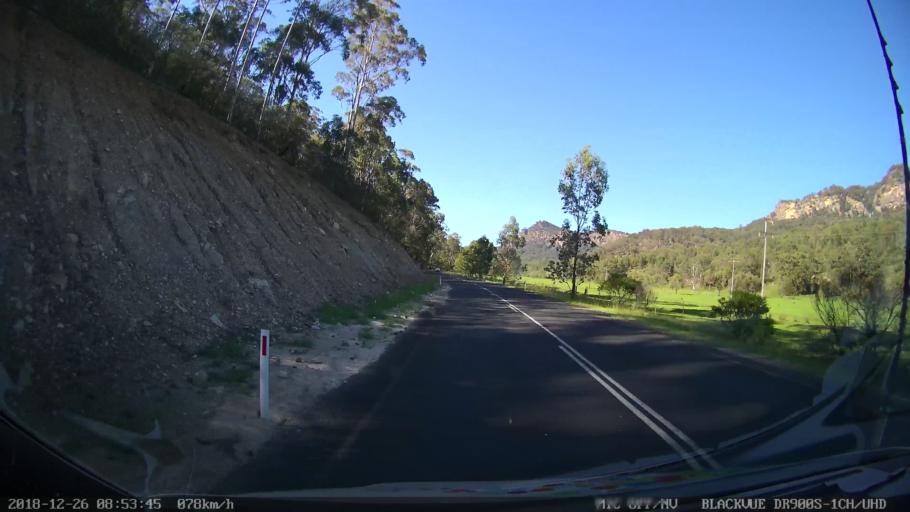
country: AU
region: New South Wales
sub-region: Mid-Western Regional
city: Kandos
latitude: -32.6077
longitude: 150.0760
